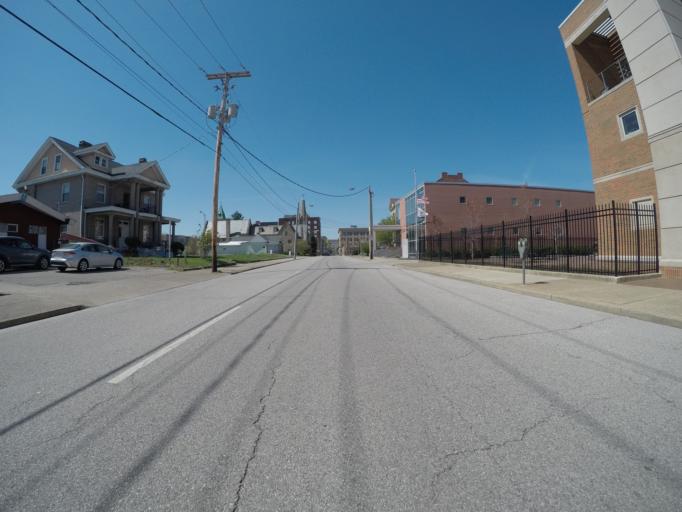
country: US
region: West Virginia
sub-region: Kanawha County
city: Charleston
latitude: 38.3465
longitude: -81.6305
